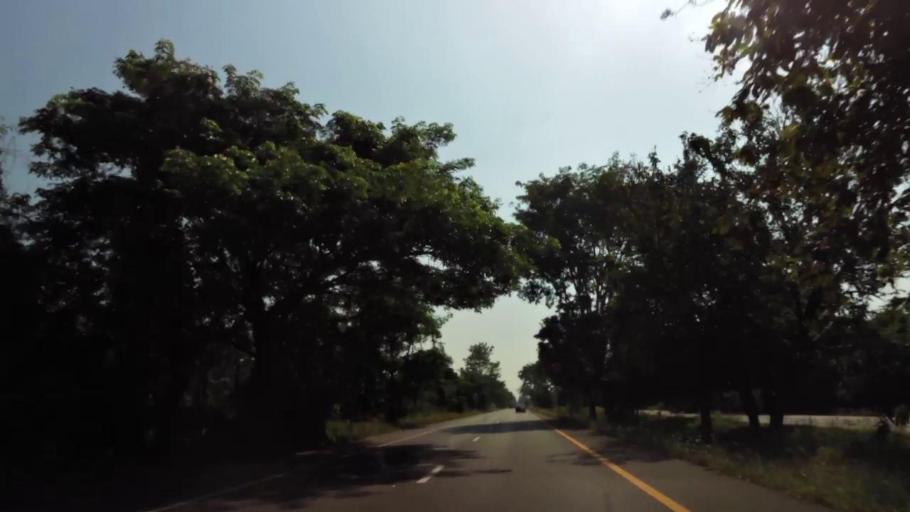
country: TH
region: Nakhon Sawan
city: Banphot Phisai
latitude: 16.0021
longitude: 100.1161
